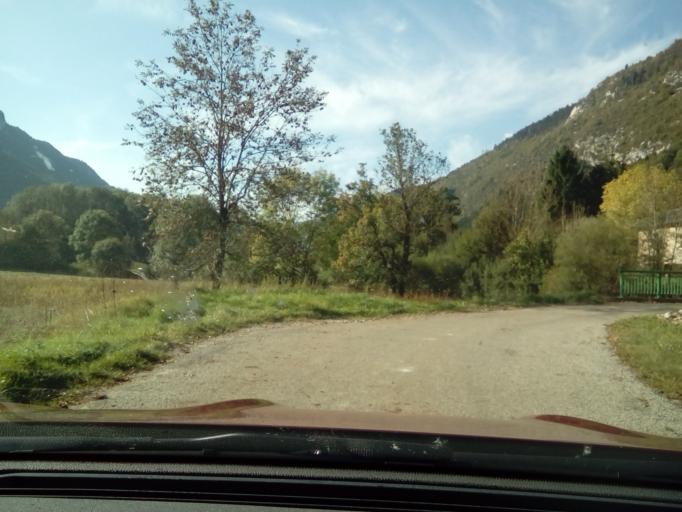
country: FR
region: Rhone-Alpes
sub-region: Departement de la Drome
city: Saint-Laurent-en-Royans
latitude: 44.9024
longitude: 5.4264
